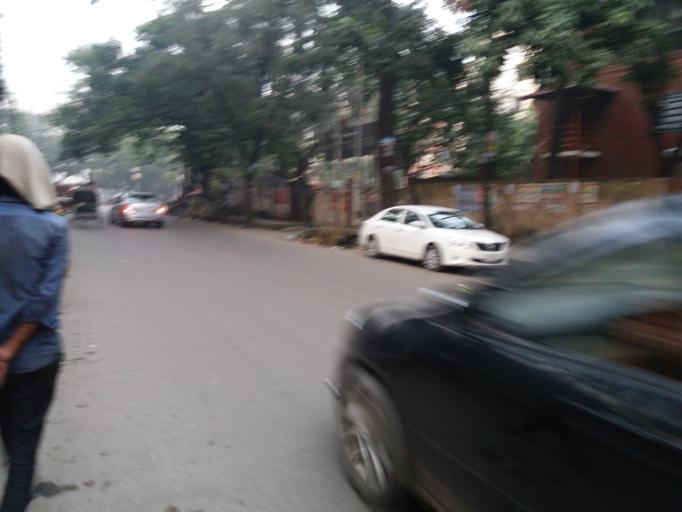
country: BD
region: Dhaka
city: Azimpur
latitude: 23.7438
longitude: 90.3799
